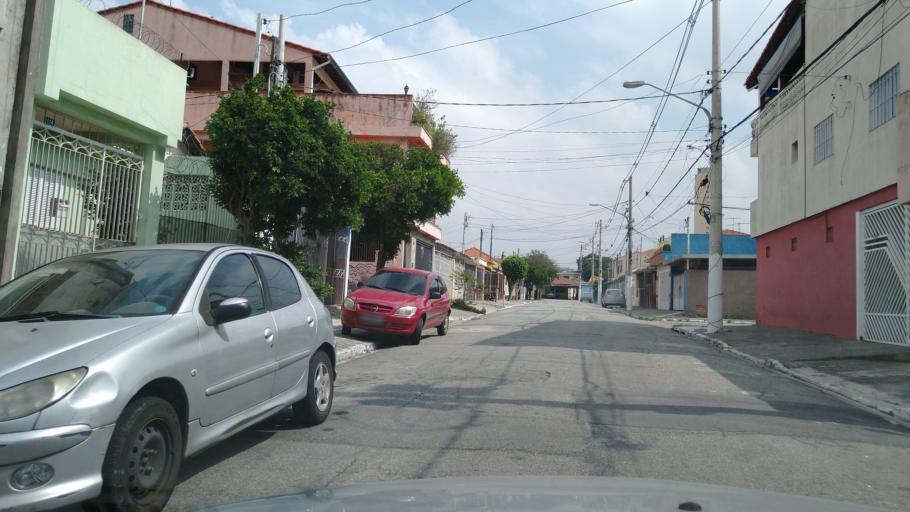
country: BR
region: Sao Paulo
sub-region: Guarulhos
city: Guarulhos
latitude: -23.4699
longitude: -46.5783
